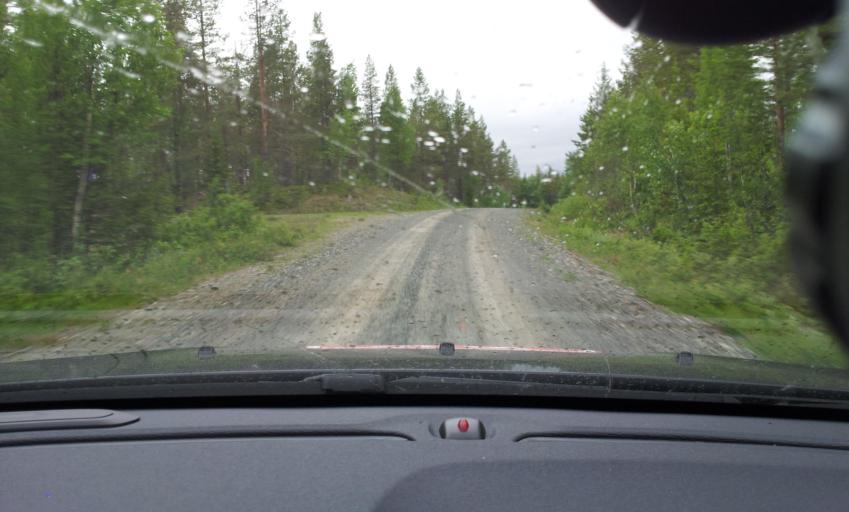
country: SE
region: Jaemtland
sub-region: Are Kommun
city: Jarpen
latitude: 63.1680
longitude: 13.5040
